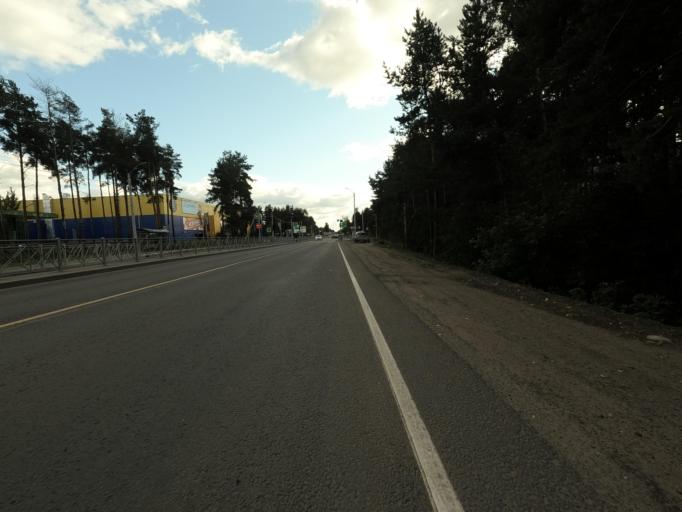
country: RU
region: Leningrad
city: Vsevolozhsk
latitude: 59.9920
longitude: 30.6583
